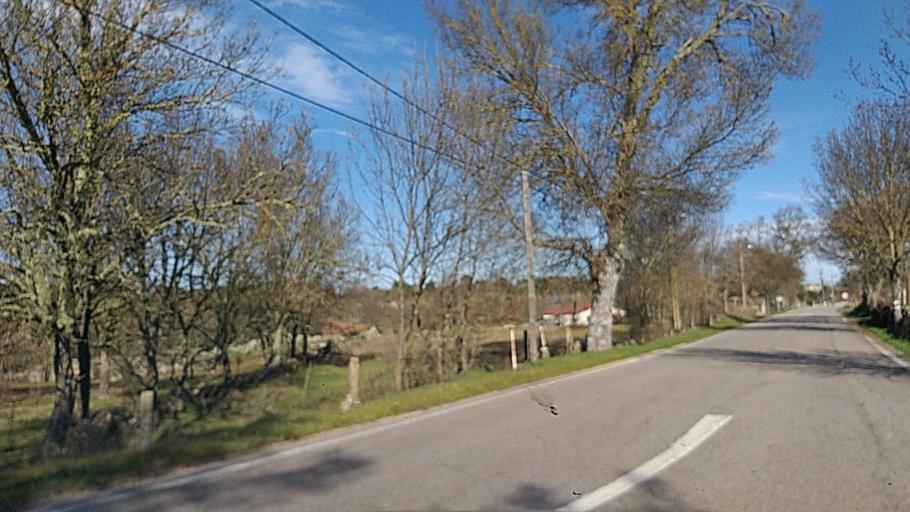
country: PT
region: Guarda
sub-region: Guarda
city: Sequeira
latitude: 40.6035
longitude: -7.0796
